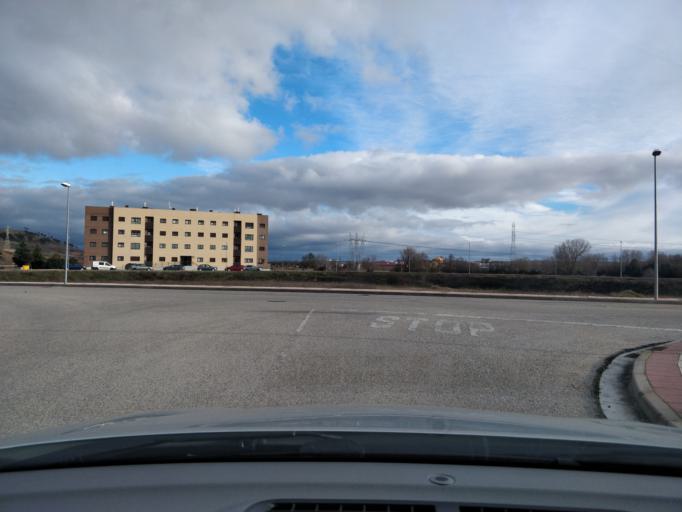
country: ES
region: Castille and Leon
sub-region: Provincia de Burgos
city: Villalbilla de Burgos
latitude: 42.3545
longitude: -3.7573
